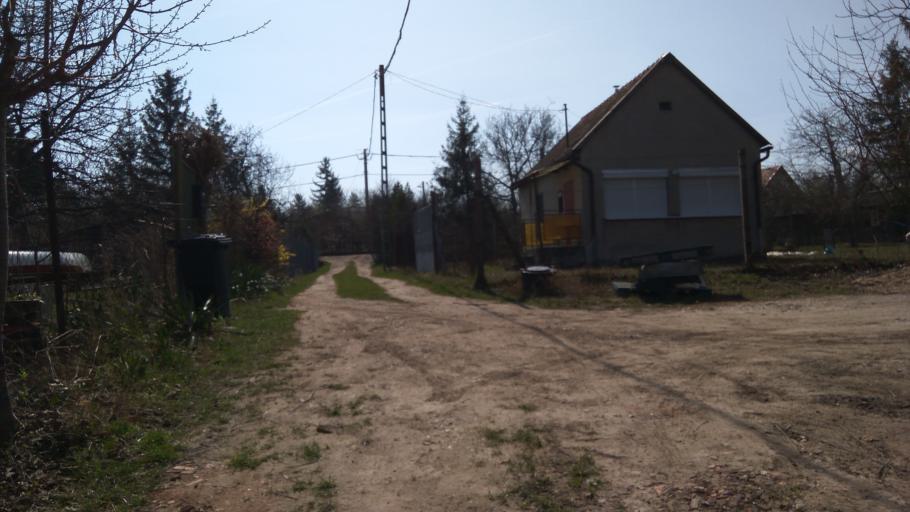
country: HU
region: Pest
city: Budakalasz
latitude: 47.6125
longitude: 19.0379
